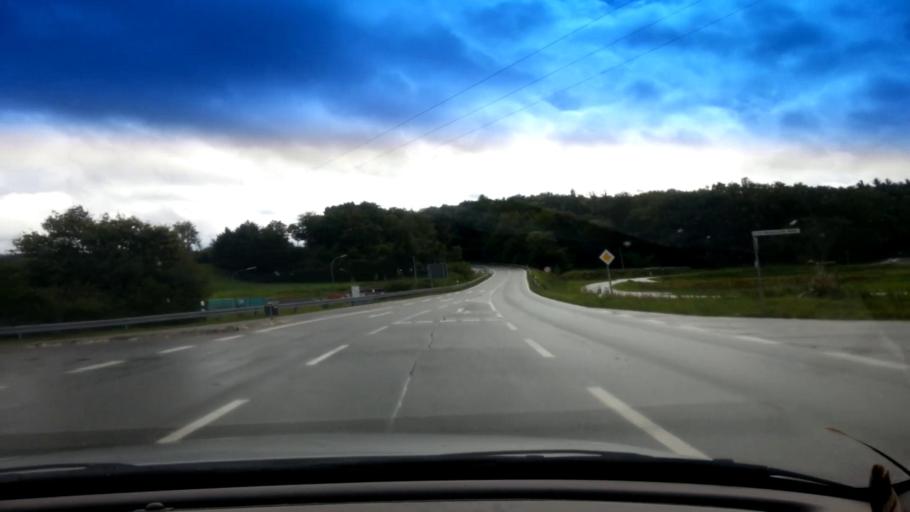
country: DE
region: Bavaria
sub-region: Upper Franconia
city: Frensdorf
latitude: 49.8503
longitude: 10.8788
